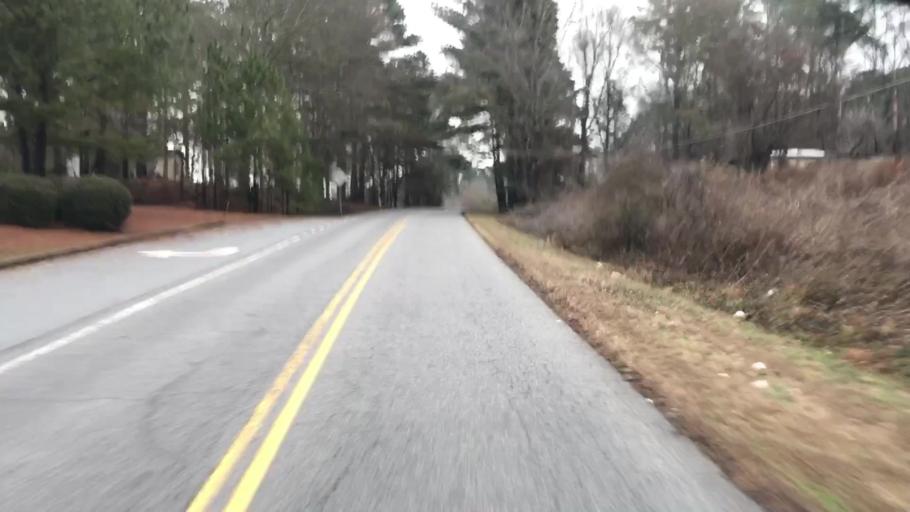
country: US
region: Georgia
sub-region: Walton County
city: Loganville
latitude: 33.7988
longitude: -83.9613
